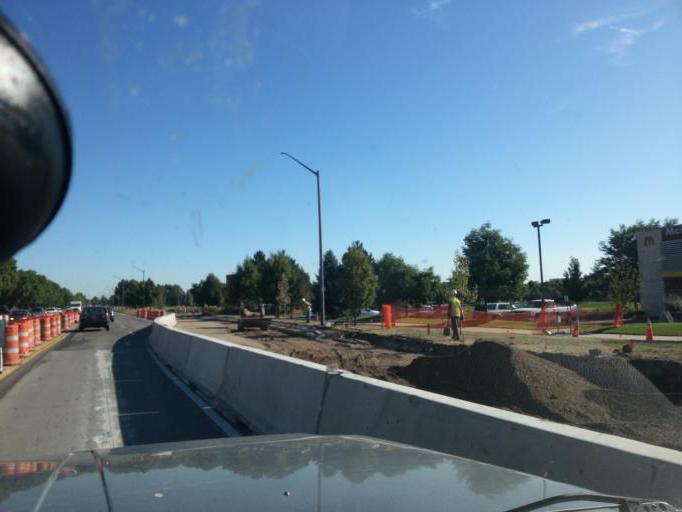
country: US
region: Colorado
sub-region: Larimer County
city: Fort Collins
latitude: 40.5382
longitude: -105.0392
